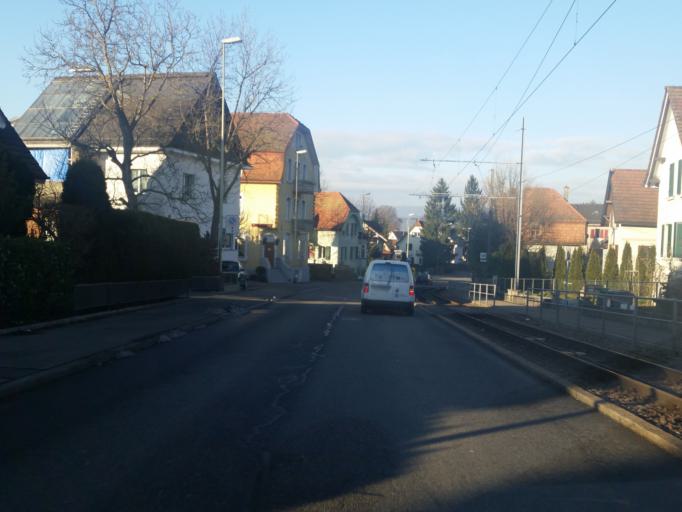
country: CH
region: Zurich
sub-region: Bezirk Dietikon
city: Dietikon / Kreuzacker
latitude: 47.3955
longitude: 8.3987
